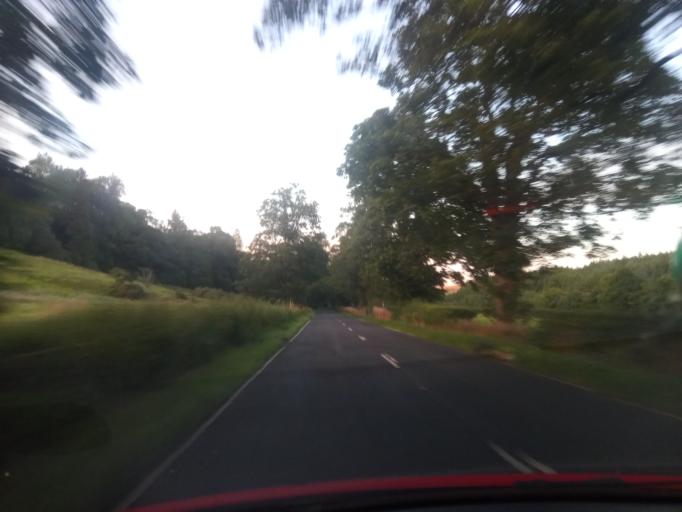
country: GB
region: England
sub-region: Northumberland
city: Bardon Mill
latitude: 54.9134
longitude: -2.3402
